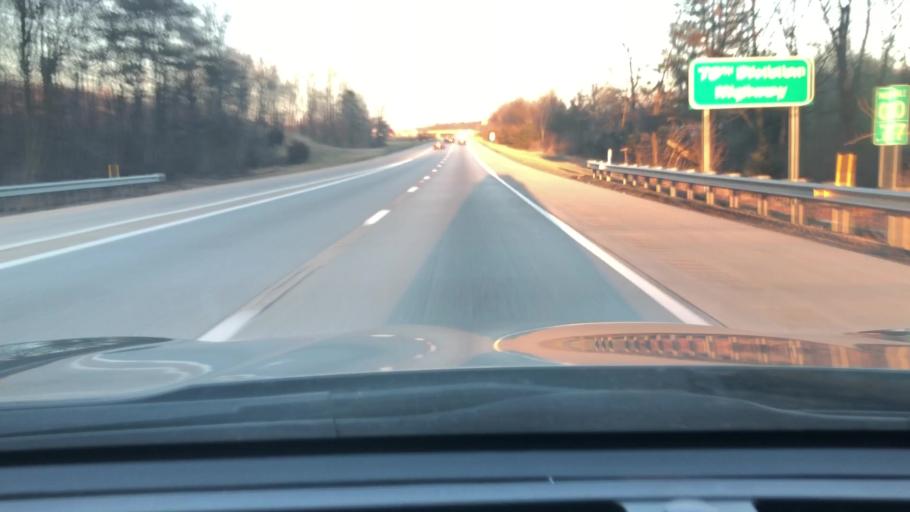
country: US
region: Pennsylvania
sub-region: Lebanon County
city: Jonestown
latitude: 40.4270
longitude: -76.5136
